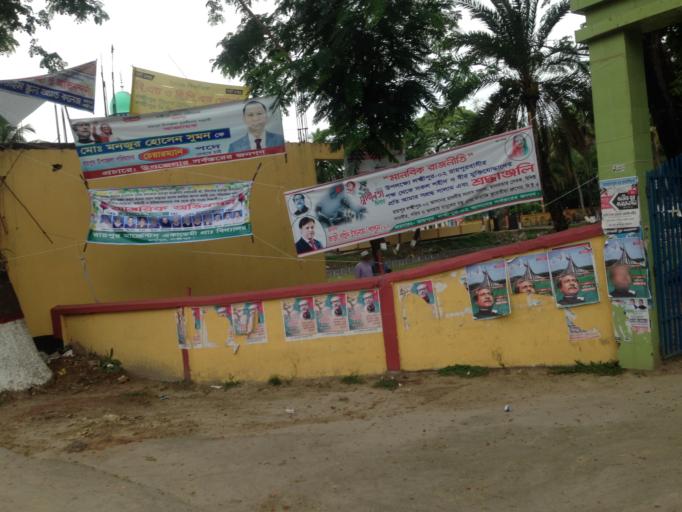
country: BD
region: Chittagong
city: Raipur
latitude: 23.0361
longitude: 90.7614
